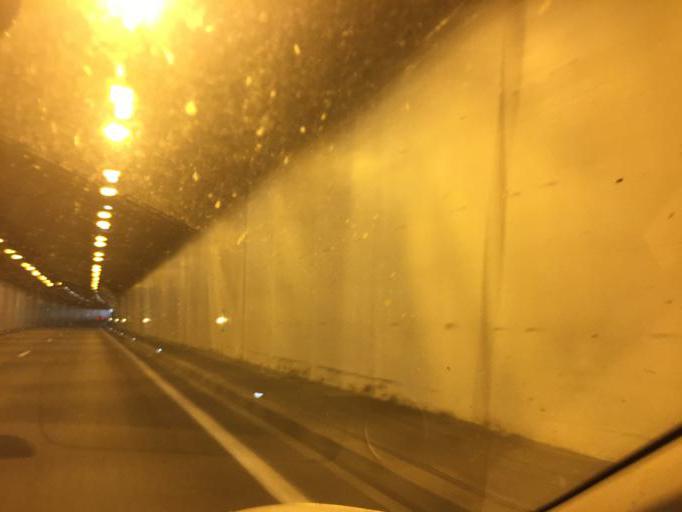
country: LU
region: Luxembourg
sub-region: Canton de Mersch
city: Mersch
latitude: 49.7413
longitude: 6.0946
